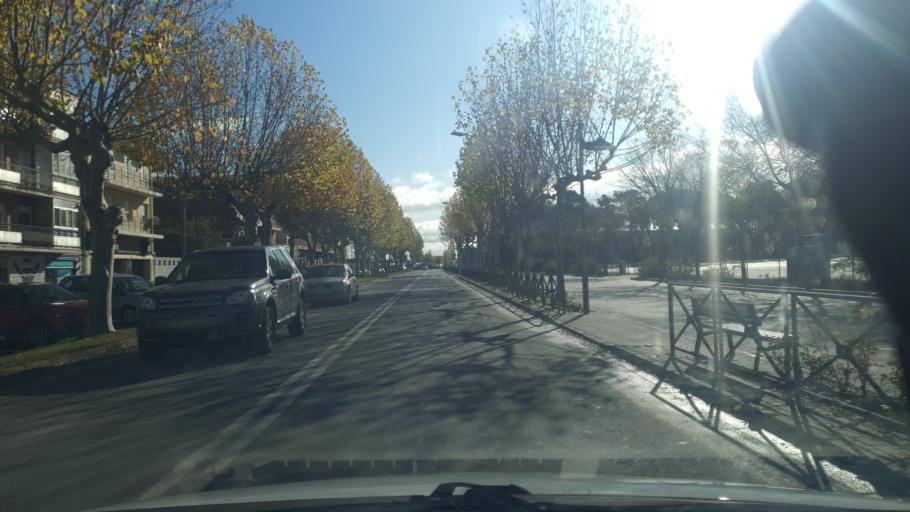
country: ES
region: Castille and Leon
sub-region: Provincia de Avila
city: Arevalo
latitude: 41.0553
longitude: -4.7130
